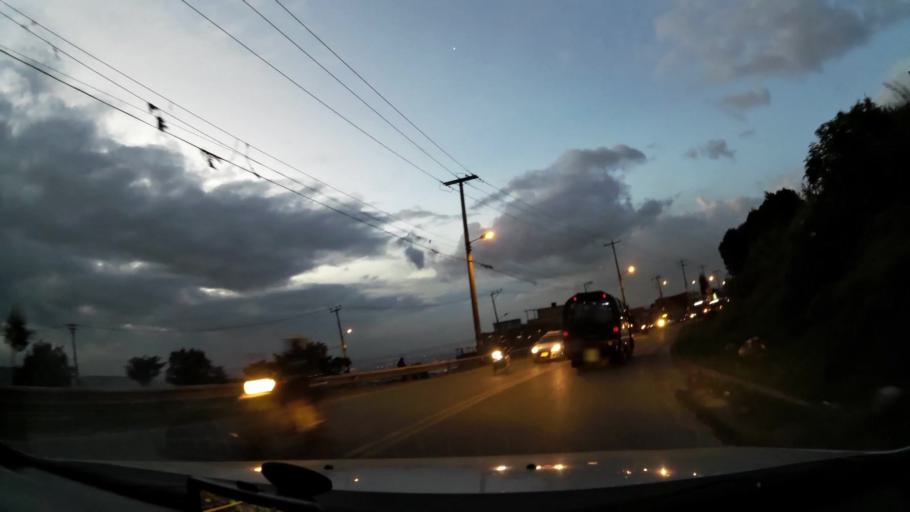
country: CO
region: Bogota D.C.
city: Bogota
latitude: 4.5495
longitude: -74.0864
